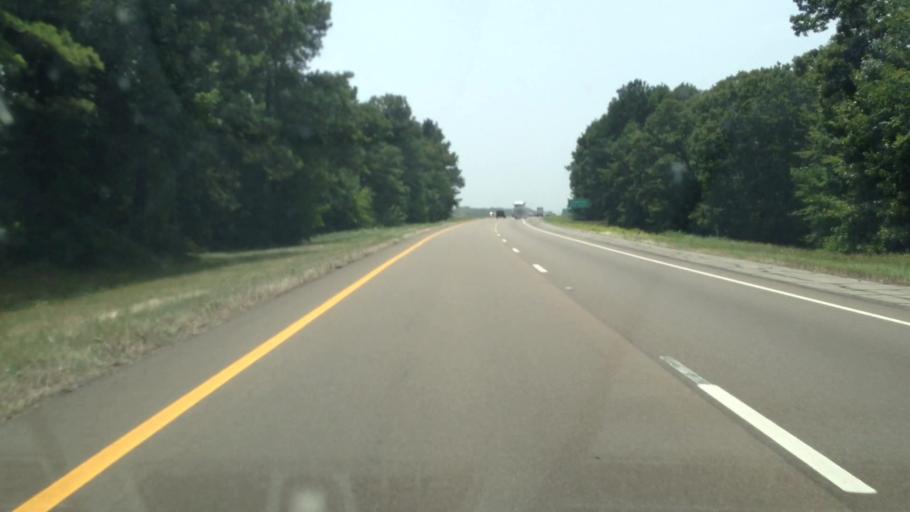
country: US
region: Texas
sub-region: Morris County
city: Naples
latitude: 33.2965
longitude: -94.7206
